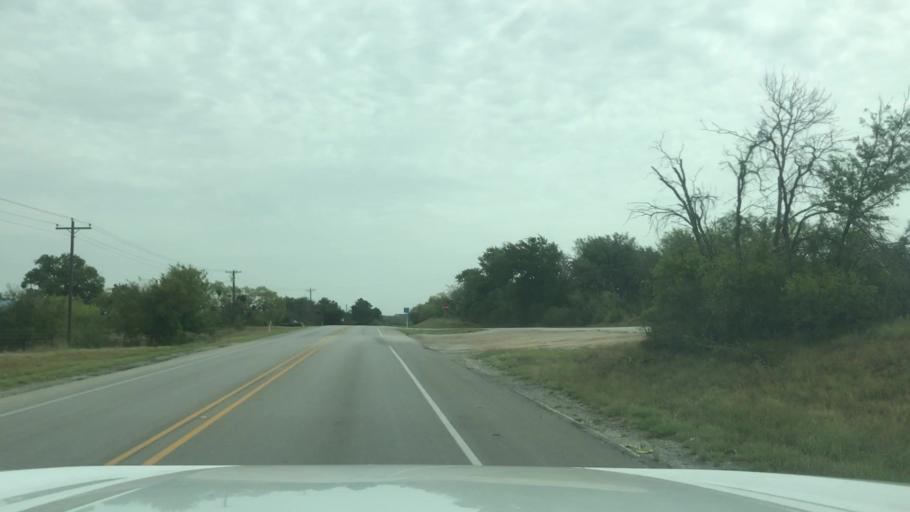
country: US
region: Texas
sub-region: Erath County
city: Dublin
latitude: 32.0948
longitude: -98.4108
